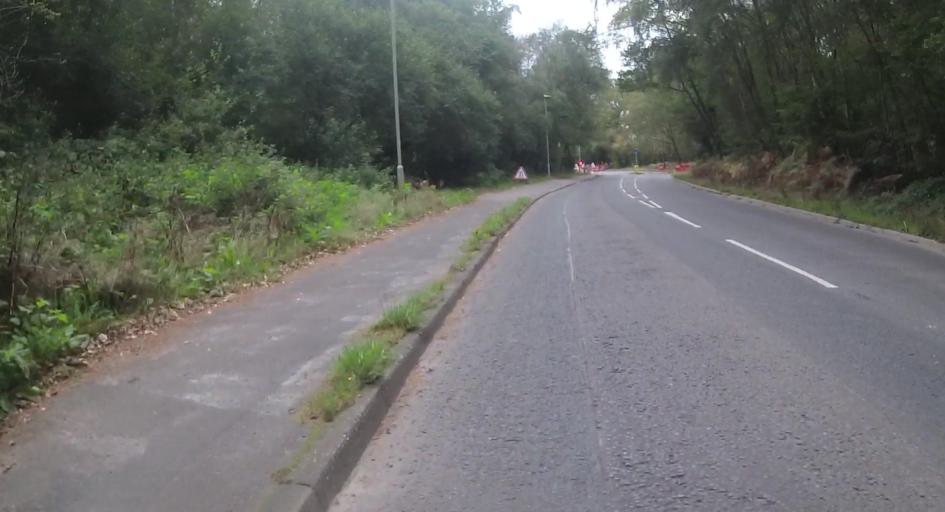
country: GB
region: England
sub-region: Hampshire
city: Fleet
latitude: 51.2757
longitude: -0.8636
